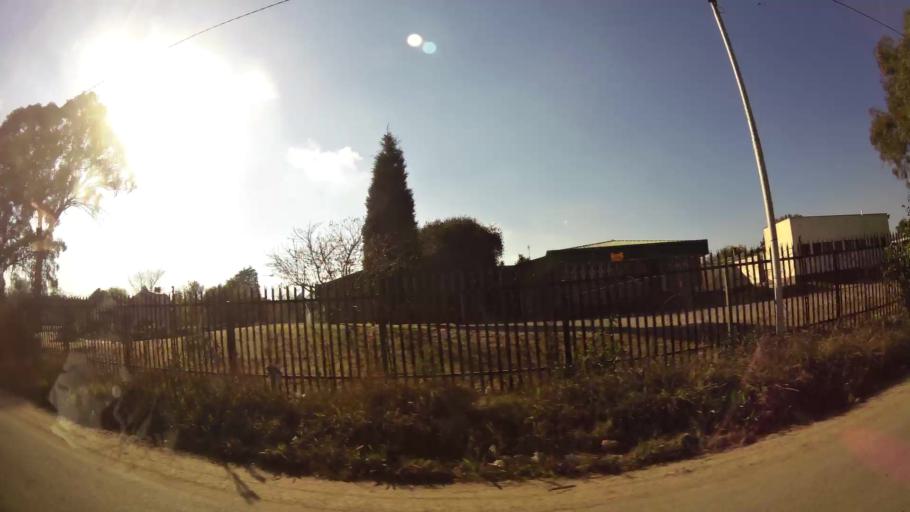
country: ZA
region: Gauteng
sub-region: City of Johannesburg Metropolitan Municipality
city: Roodepoort
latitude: -26.1585
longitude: 27.8578
